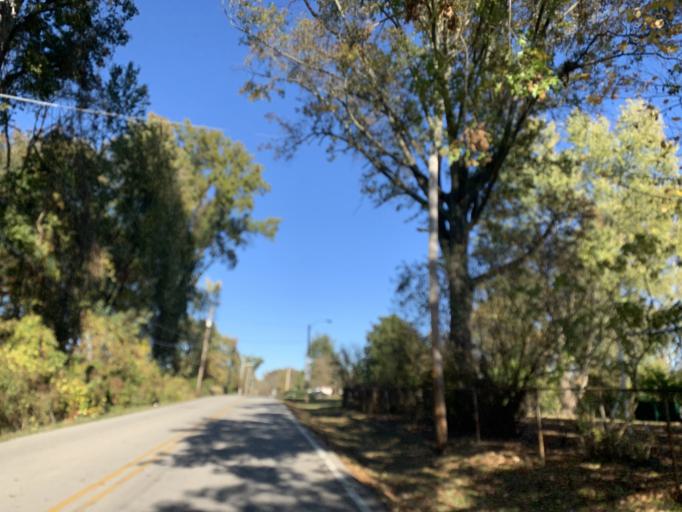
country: US
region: Kentucky
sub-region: Jefferson County
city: Pleasure Ridge Park
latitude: 38.1455
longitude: -85.8826
